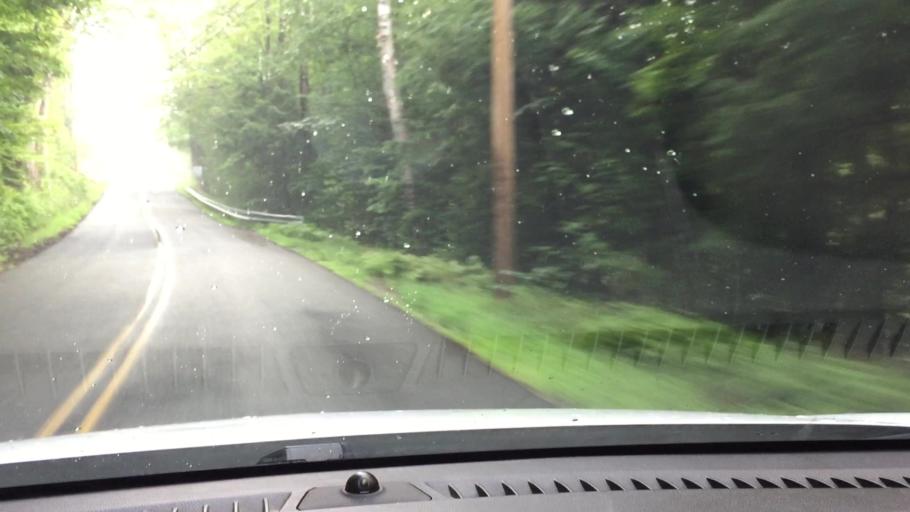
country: US
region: Massachusetts
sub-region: Berkshire County
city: Becket
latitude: 42.4171
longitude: -72.9830
